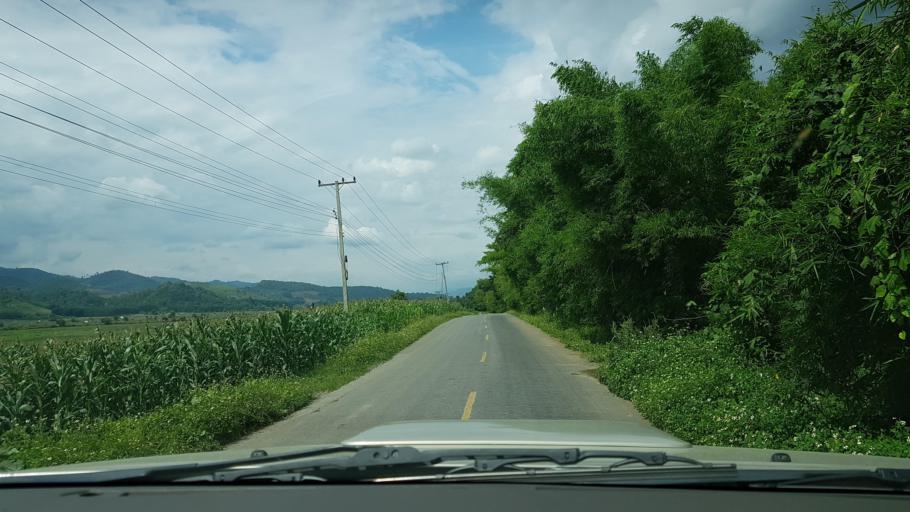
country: LA
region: Loungnamtha
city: Muang Nale
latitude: 20.2696
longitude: 101.6009
